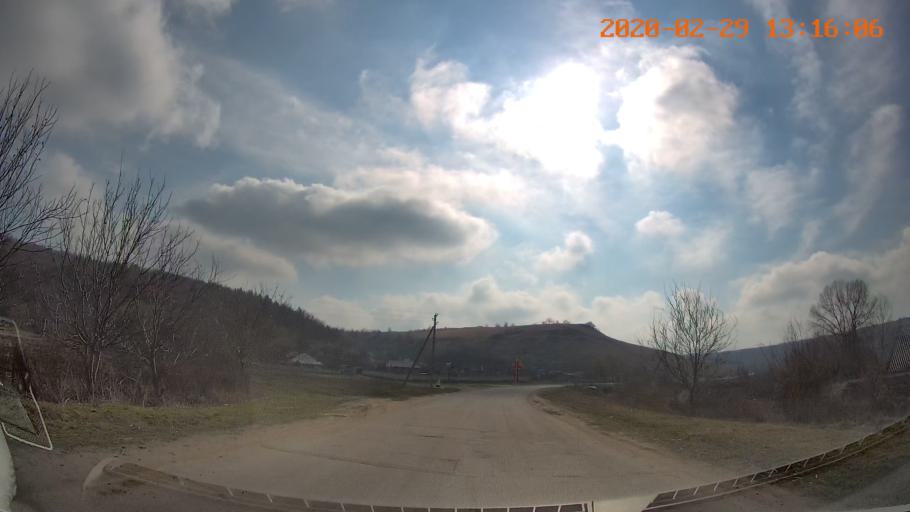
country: MD
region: Telenesti
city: Camenca
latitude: 48.0051
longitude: 28.6665
